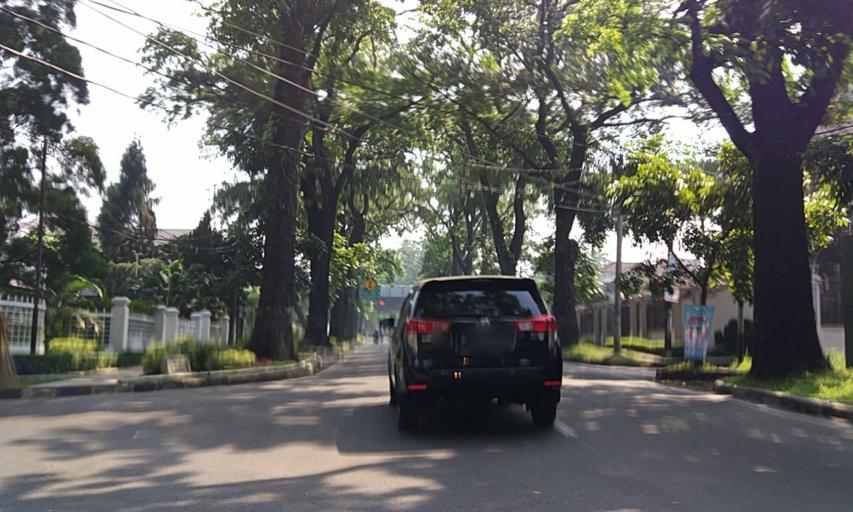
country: ID
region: West Java
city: Bandung
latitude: -6.9018
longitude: 107.6024
